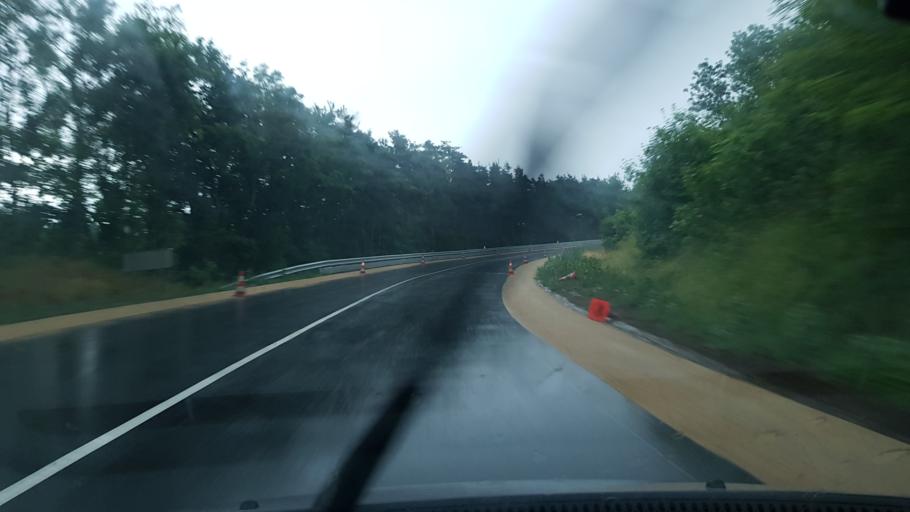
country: FR
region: Auvergne
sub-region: Departement de la Haute-Loire
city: Saint-Paulien
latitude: 45.1051
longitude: 3.8070
